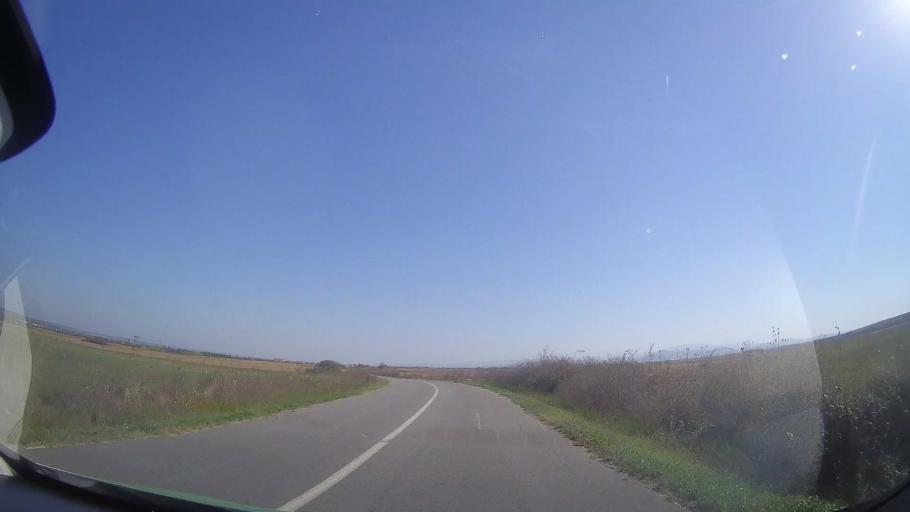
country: RO
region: Timis
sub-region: Comuna Bethausen
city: Bethausen
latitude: 45.7939
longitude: 21.9748
